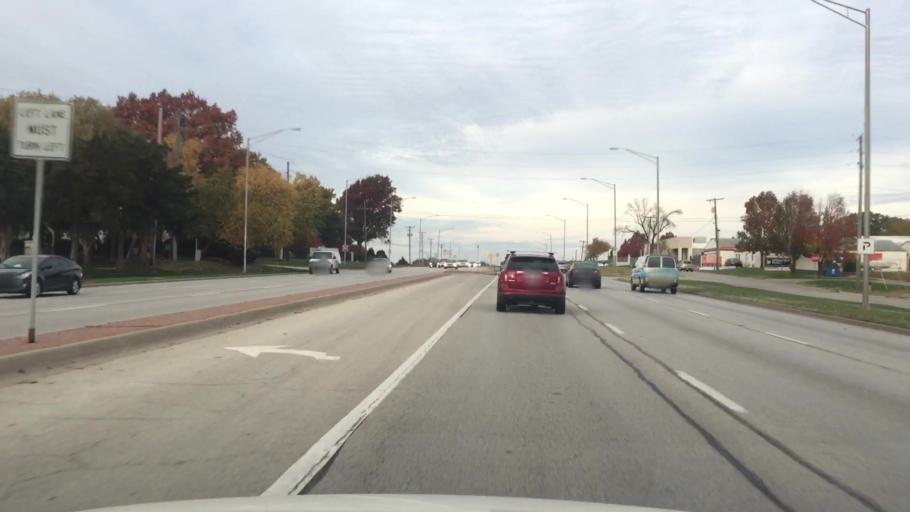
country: US
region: Kansas
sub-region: Johnson County
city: Shawnee
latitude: 39.0148
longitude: -94.7324
